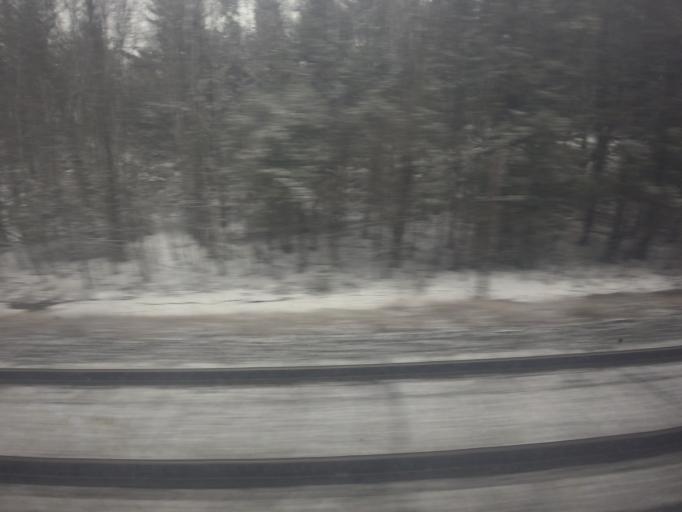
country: CA
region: Ontario
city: Brockville
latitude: 44.5468
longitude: -75.8025
